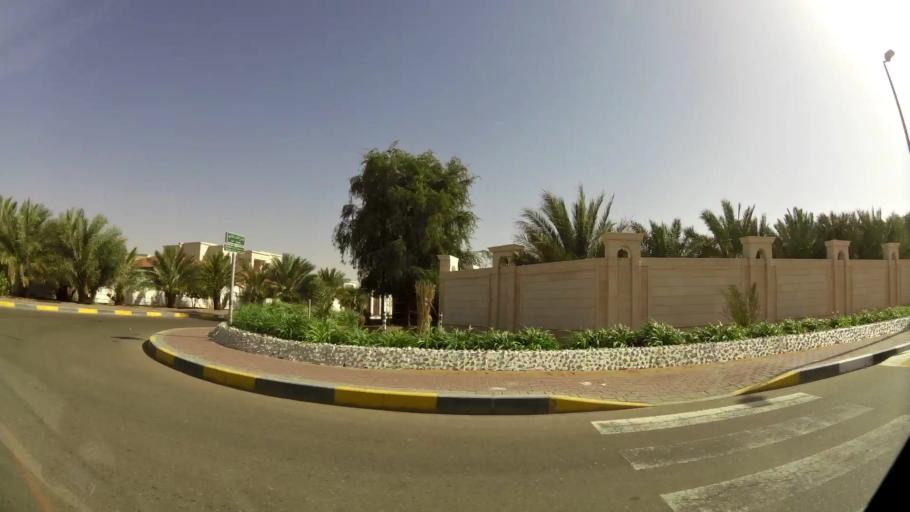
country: OM
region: Al Buraimi
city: Al Buraymi
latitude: 24.3331
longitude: 55.7902
